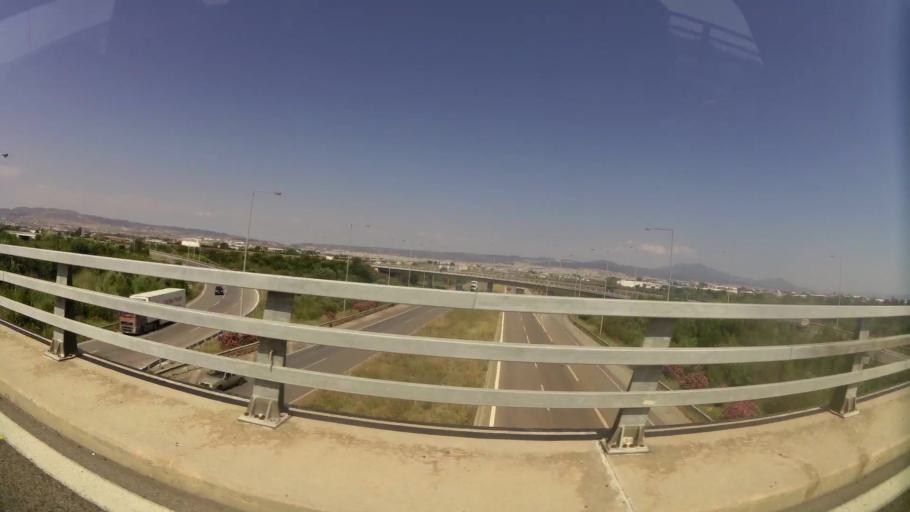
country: GR
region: Central Macedonia
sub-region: Nomos Thessalonikis
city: Kalochori
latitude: 40.6528
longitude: 22.8406
